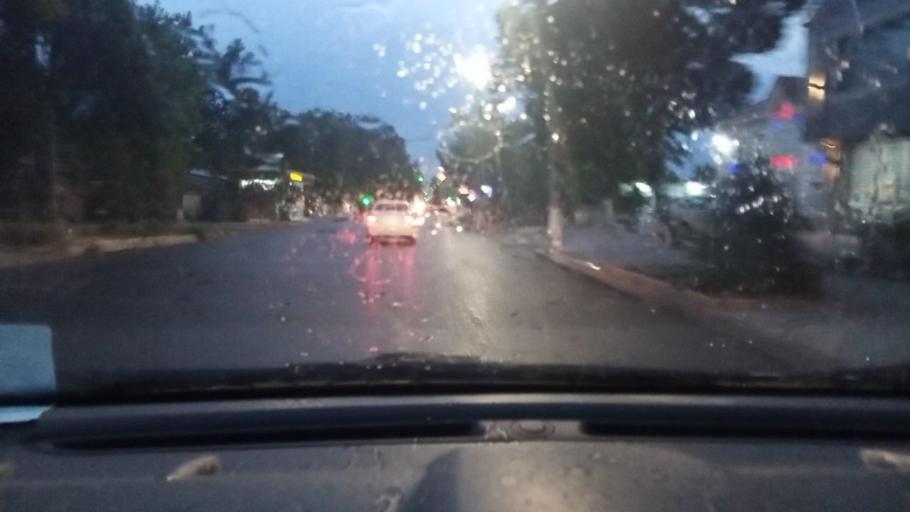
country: UZ
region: Toshkent
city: Salor
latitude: 41.3199
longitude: 69.3421
